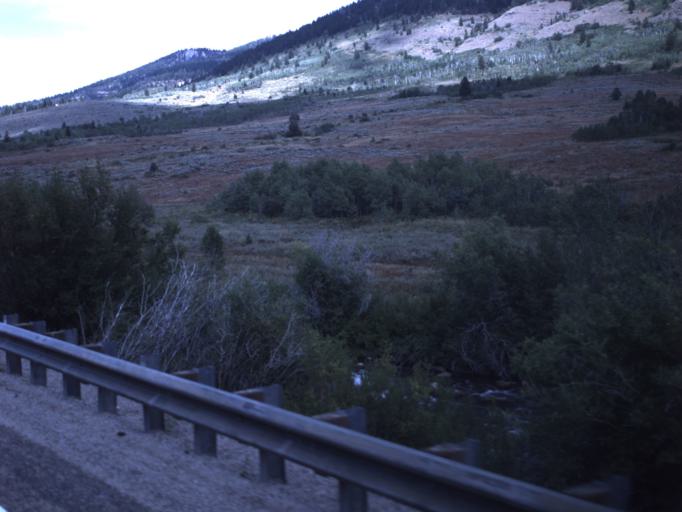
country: US
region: Utah
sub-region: Cache County
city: Richmond
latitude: 41.8961
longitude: -111.5649
